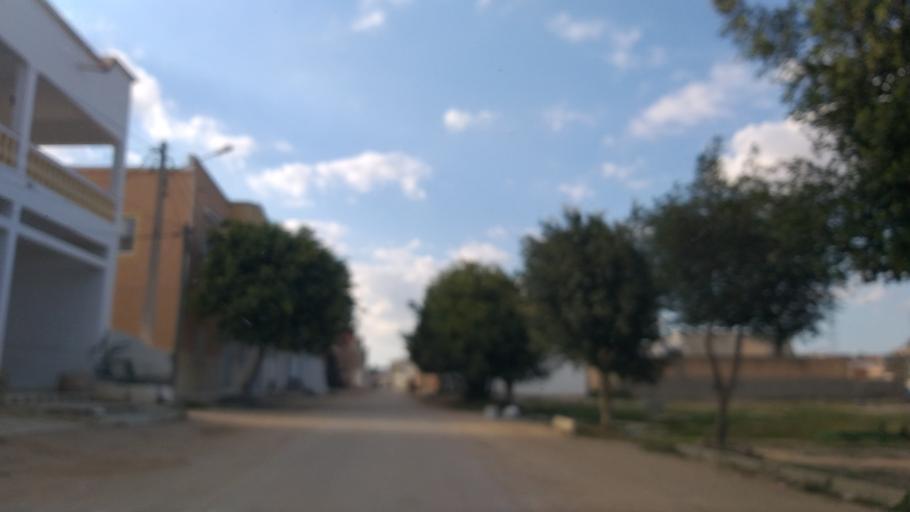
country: TN
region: Al Mahdiyah
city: El Jem
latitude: 35.3042
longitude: 10.7017
